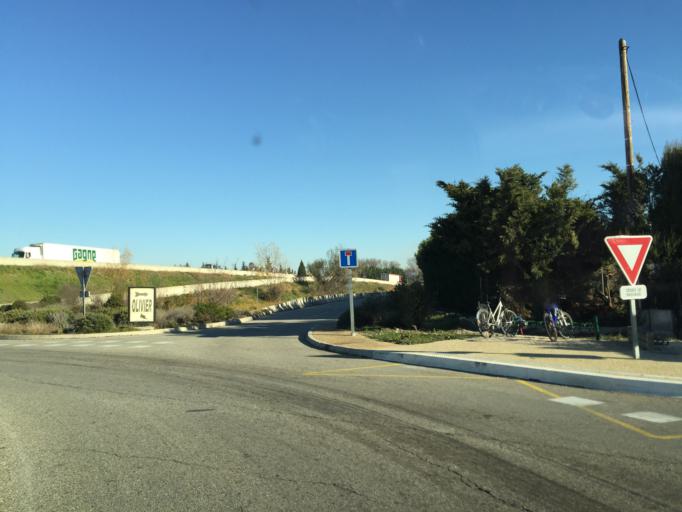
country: FR
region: Provence-Alpes-Cote d'Azur
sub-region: Departement du Vaucluse
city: Althen-des-Paluds
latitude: 44.0128
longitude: 4.9549
